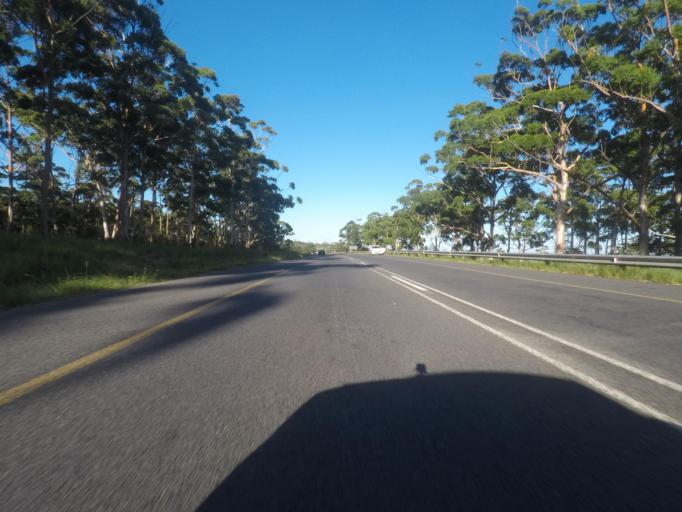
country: ZA
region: Eastern Cape
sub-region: Buffalo City Metropolitan Municipality
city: East London
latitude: -33.0457
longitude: 27.8250
